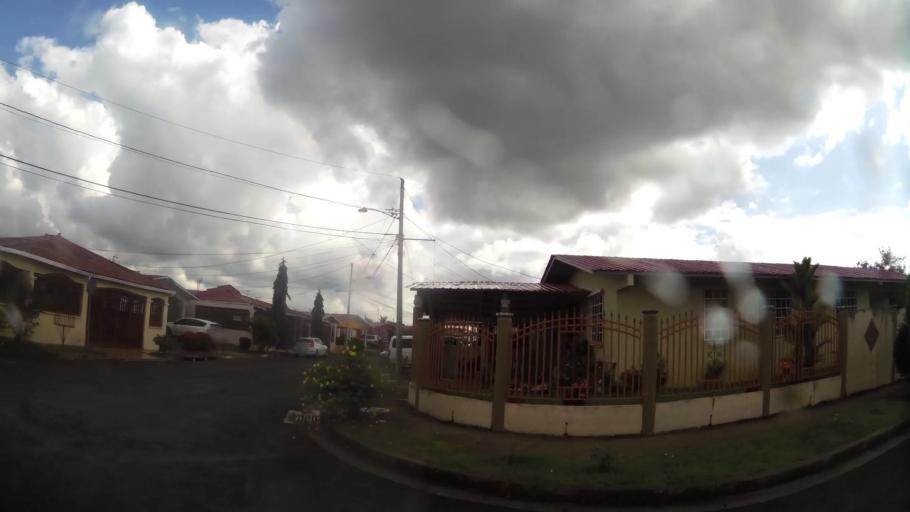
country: PA
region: Panama
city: Nuevo Arraijan
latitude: 8.9395
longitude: -79.7392
